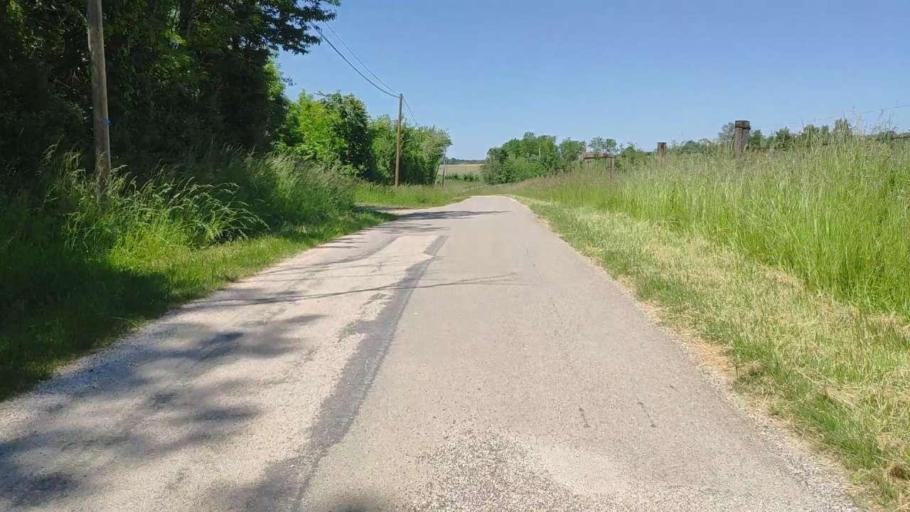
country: FR
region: Franche-Comte
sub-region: Departement du Jura
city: Bletterans
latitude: 46.7473
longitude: 5.4280
